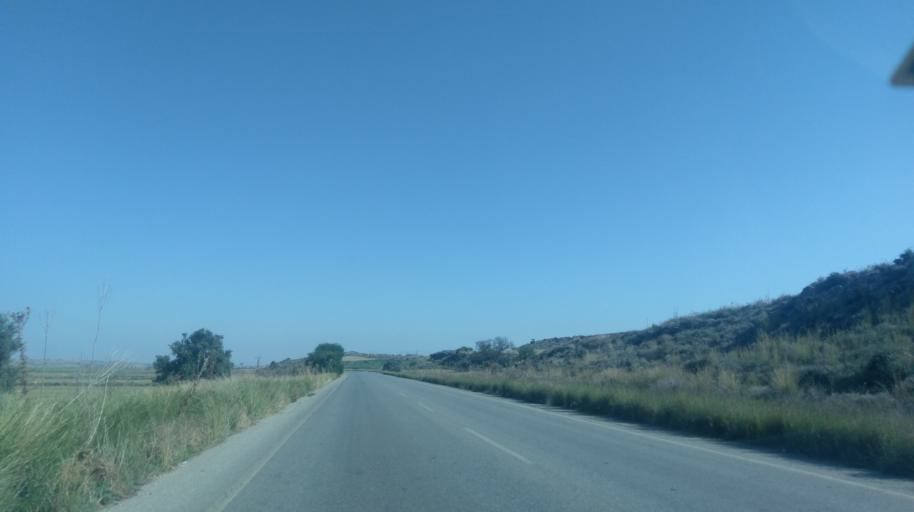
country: CY
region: Ammochostos
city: Lefkonoiko
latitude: 35.2676
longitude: 33.8066
